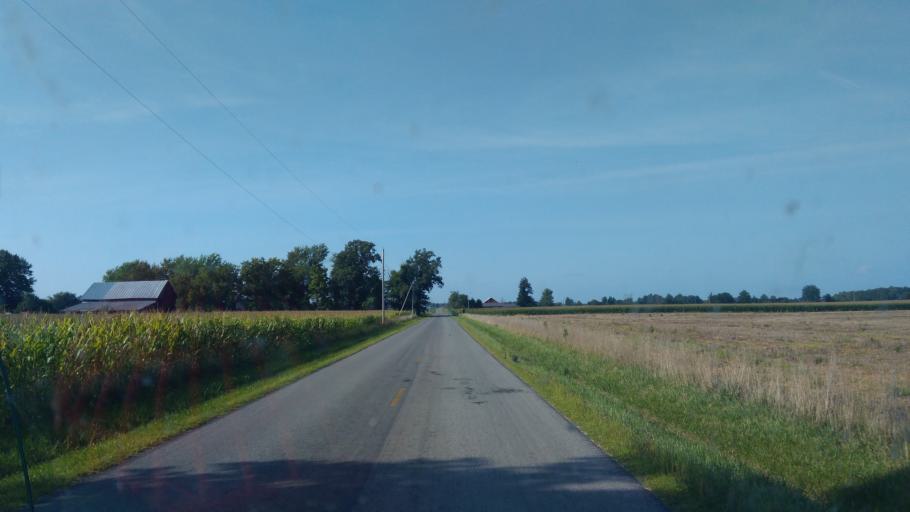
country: US
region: Ohio
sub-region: Hardin County
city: Forest
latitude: 40.8432
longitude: -83.4190
